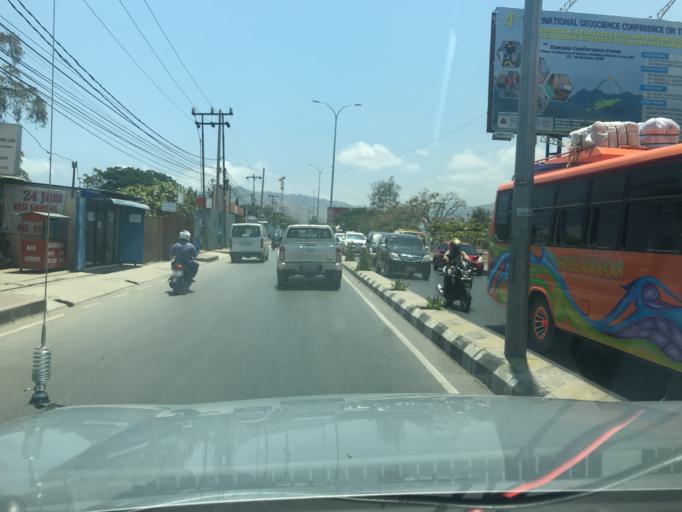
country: TL
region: Dili
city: Dili
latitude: -8.5541
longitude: 125.5649
